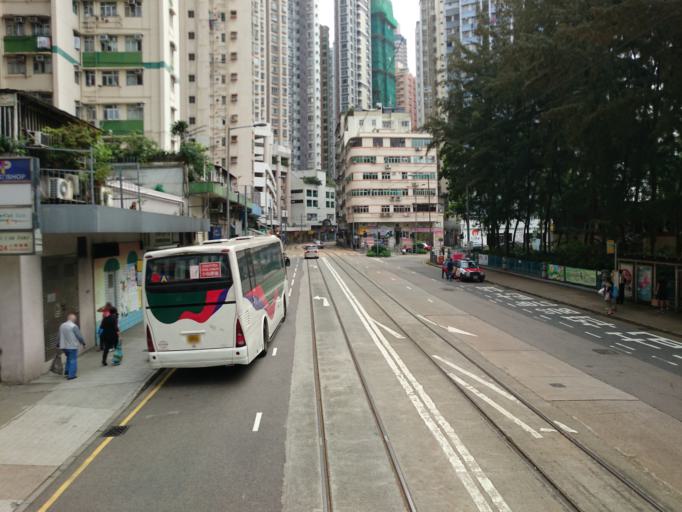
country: HK
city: Hong Kong
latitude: 22.2844
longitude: 114.1304
